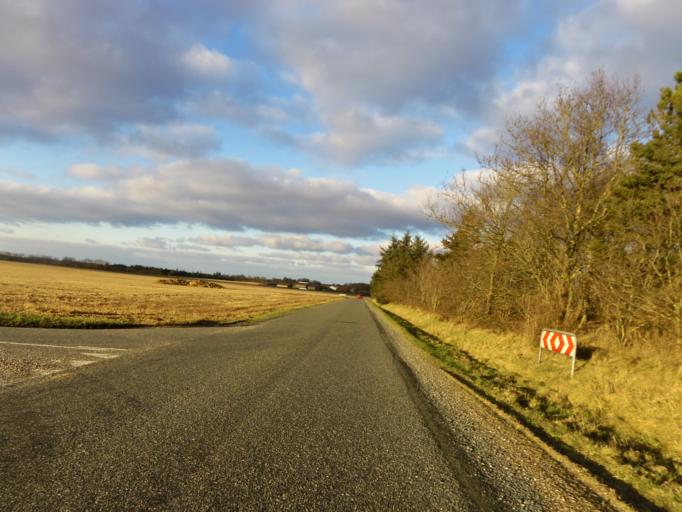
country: DK
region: South Denmark
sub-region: Esbjerg Kommune
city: Ribe
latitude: 55.2986
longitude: 8.8485
